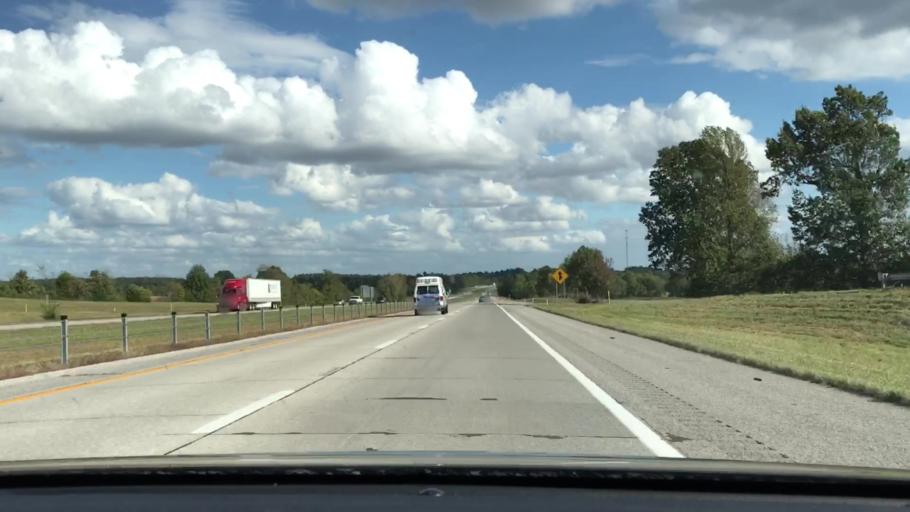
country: US
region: Kentucky
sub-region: Trigg County
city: Cadiz
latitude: 36.9657
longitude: -87.8721
